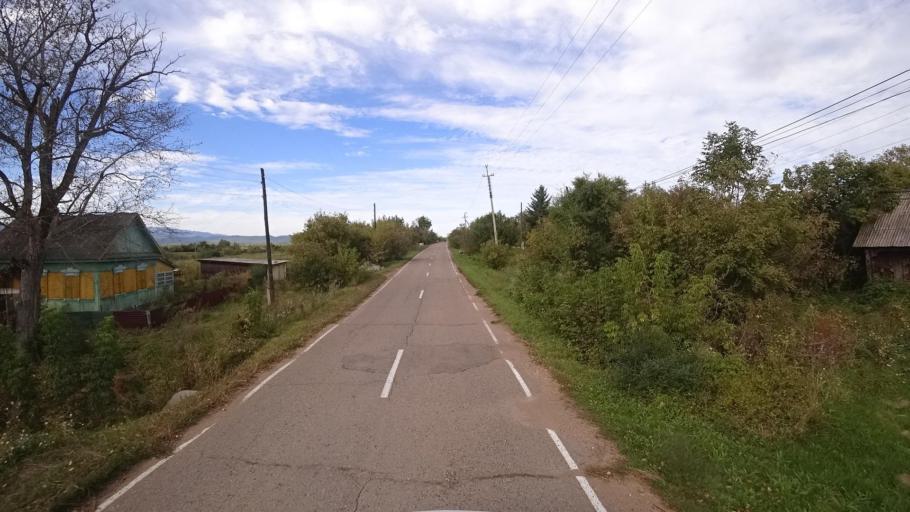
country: RU
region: Primorskiy
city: Dostoyevka
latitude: 44.3237
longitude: 133.4766
